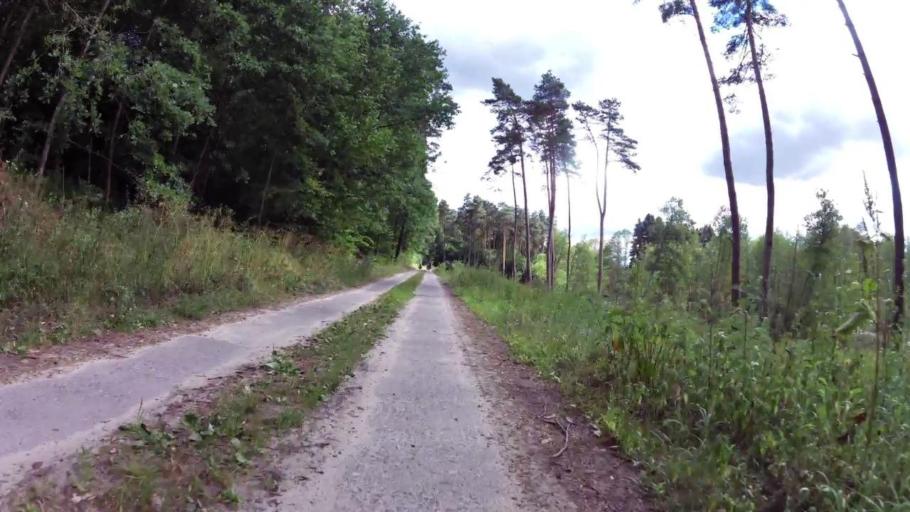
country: PL
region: West Pomeranian Voivodeship
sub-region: Powiat lobeski
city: Lobez
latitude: 53.6481
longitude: 15.5806
